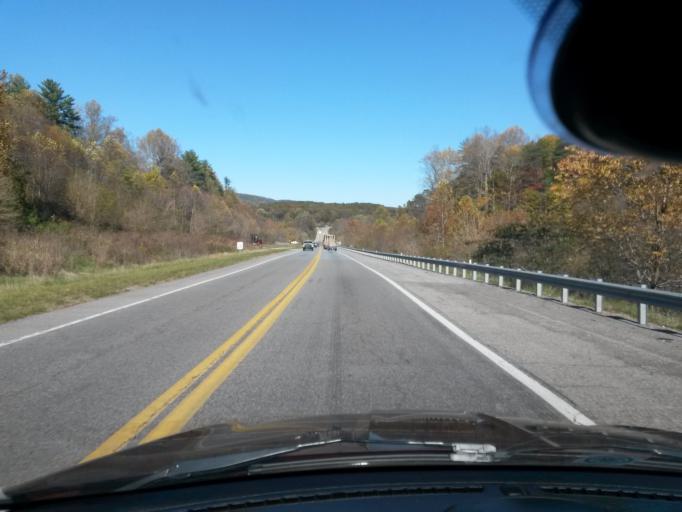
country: US
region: Virginia
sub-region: Alleghany County
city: Clifton Forge
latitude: 37.7690
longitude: -79.7829
